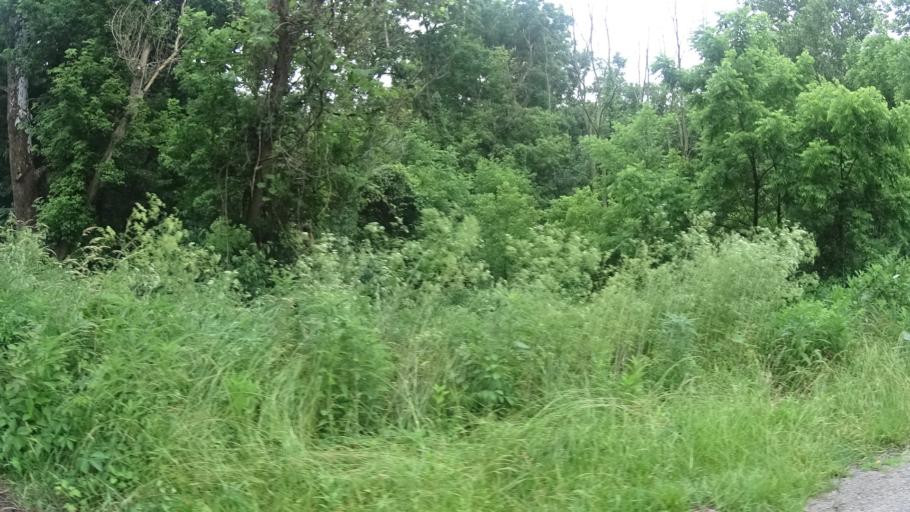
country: US
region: Ohio
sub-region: Erie County
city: Milan
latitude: 41.3349
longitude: -82.5768
